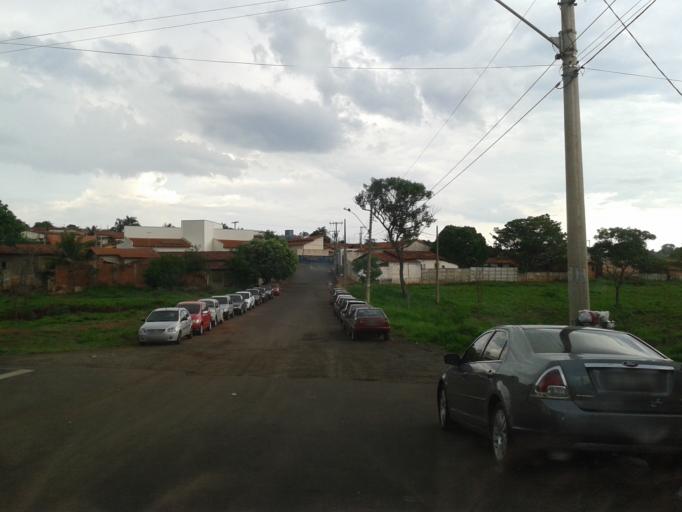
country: BR
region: Minas Gerais
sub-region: Ituiutaba
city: Ituiutaba
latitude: -18.9680
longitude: -49.4692
